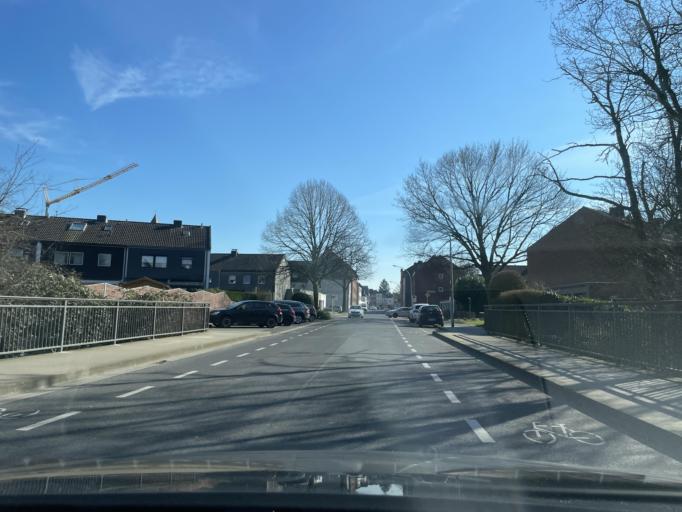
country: DE
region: North Rhine-Westphalia
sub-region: Regierungsbezirk Dusseldorf
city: Monchengladbach
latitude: 51.2067
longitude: 6.4100
